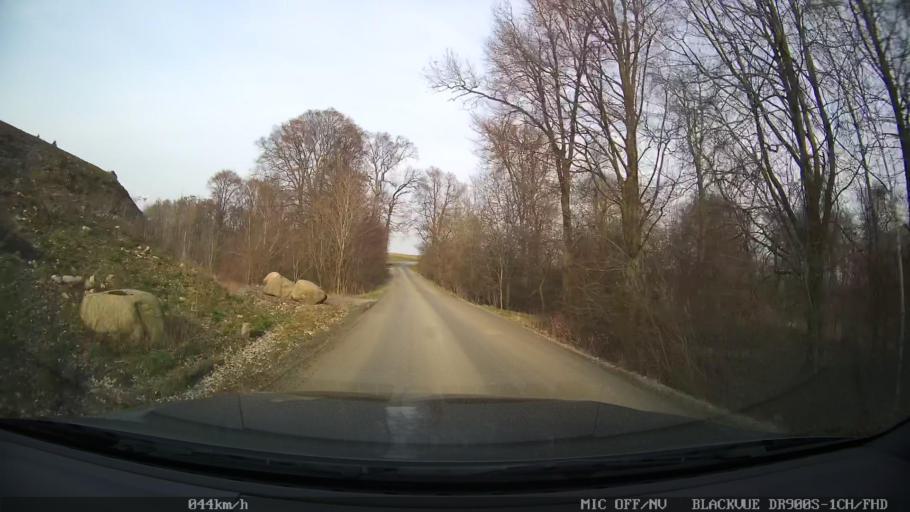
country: SE
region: Skane
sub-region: Ystads Kommun
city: Ystad
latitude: 55.4585
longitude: 13.7816
